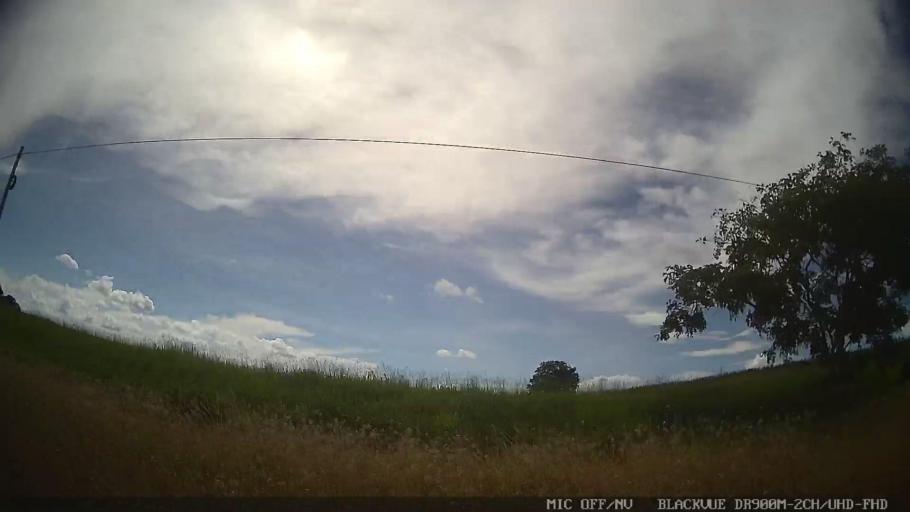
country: BR
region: Sao Paulo
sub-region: Conchas
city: Conchas
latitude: -22.9748
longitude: -47.9872
